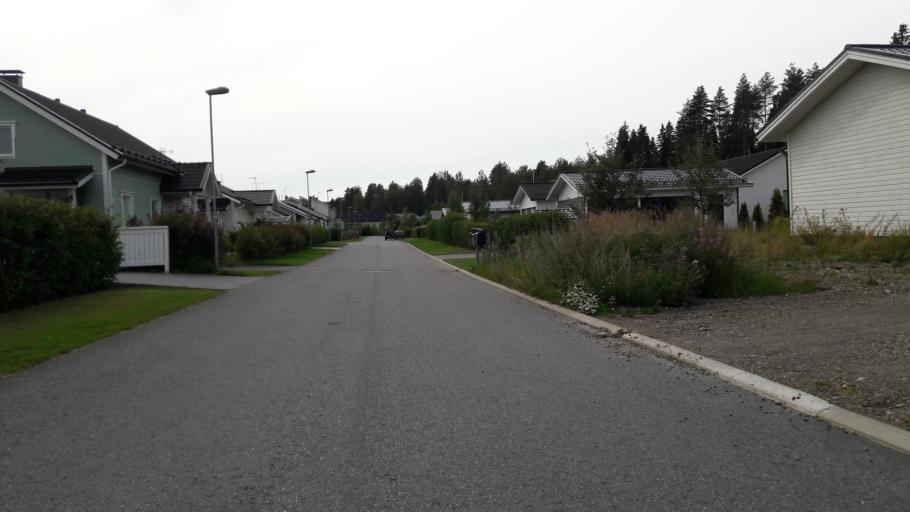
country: FI
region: North Karelia
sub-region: Joensuu
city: Joensuu
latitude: 62.5737
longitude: 29.8231
